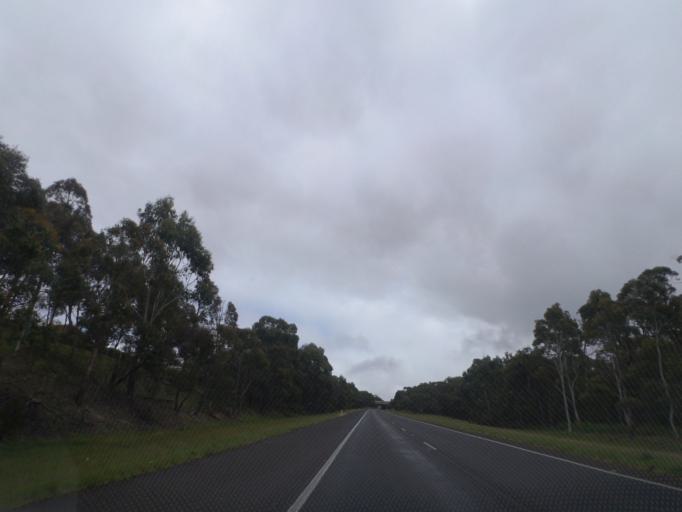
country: AU
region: Victoria
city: Brown Hill
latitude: -37.5407
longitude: 143.8847
